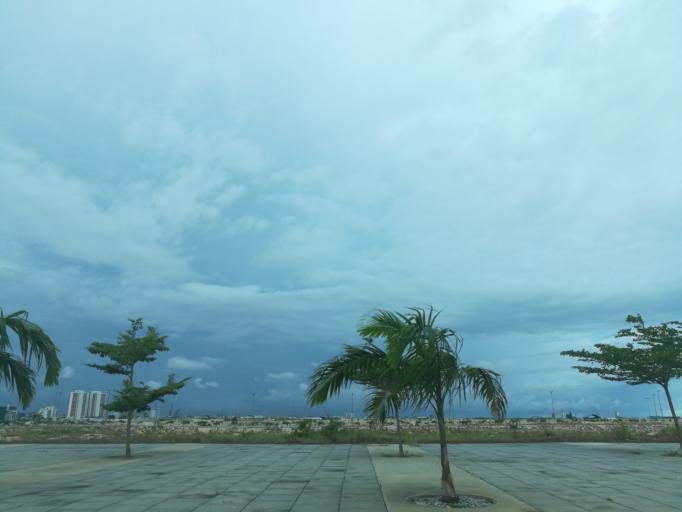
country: NG
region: Lagos
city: Ikoyi
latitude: 6.4106
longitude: 3.4174
